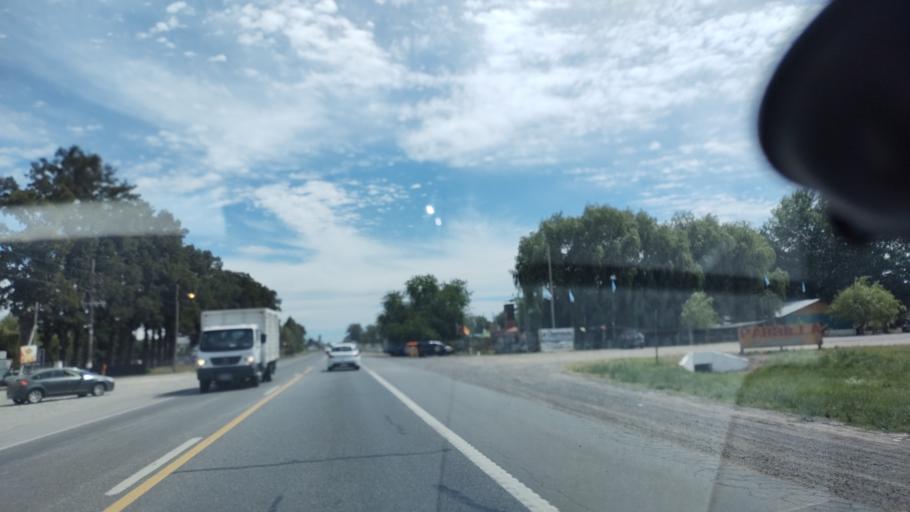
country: AR
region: Buenos Aires
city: Canuelas
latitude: -35.0367
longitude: -58.7571
